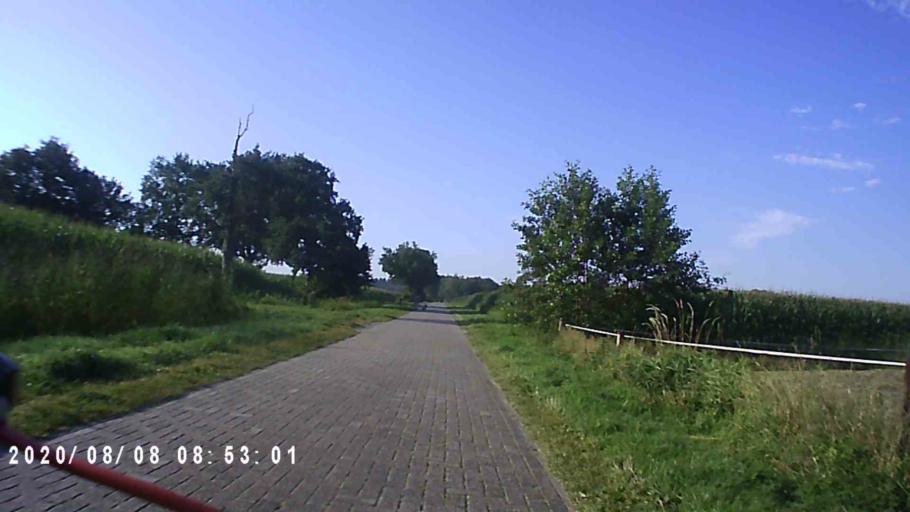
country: NL
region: Groningen
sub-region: Gemeente Leek
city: Leek
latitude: 53.0630
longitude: 6.3259
